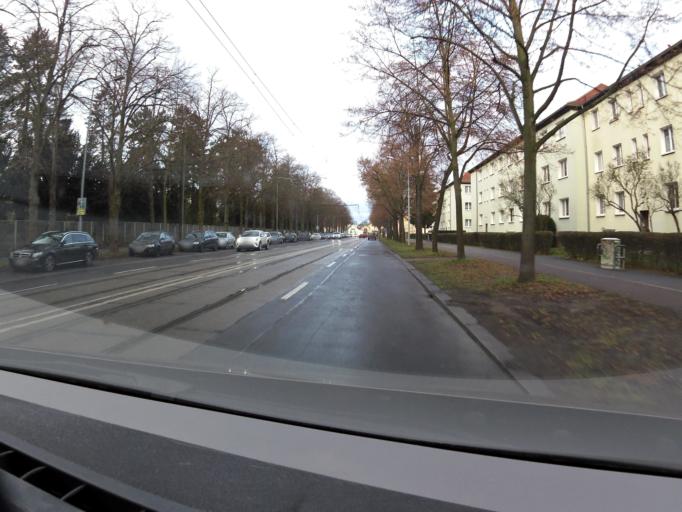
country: DE
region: Saxony-Anhalt
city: Diesdorf
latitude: 52.1289
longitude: 11.5790
